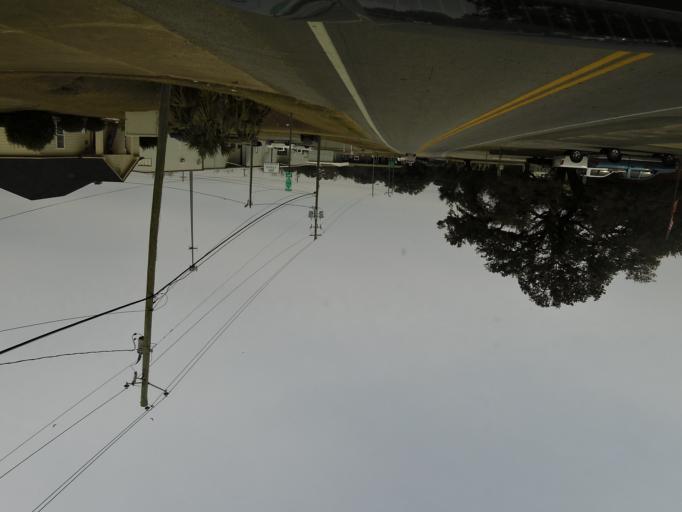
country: US
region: Georgia
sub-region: Decatur County
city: Bainbridge
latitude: 30.9148
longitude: -84.5924
